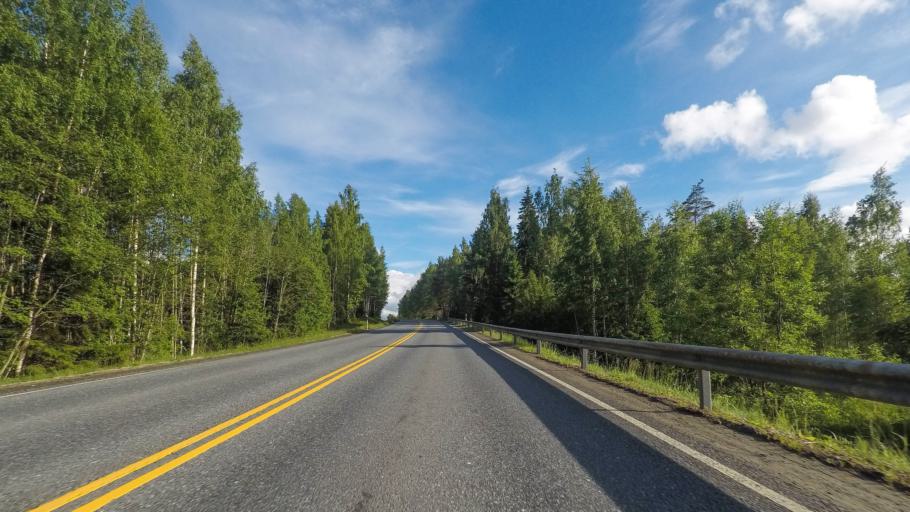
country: FI
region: Paijanne Tavastia
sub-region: Lahti
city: Hartola
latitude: 61.6573
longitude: 26.0272
